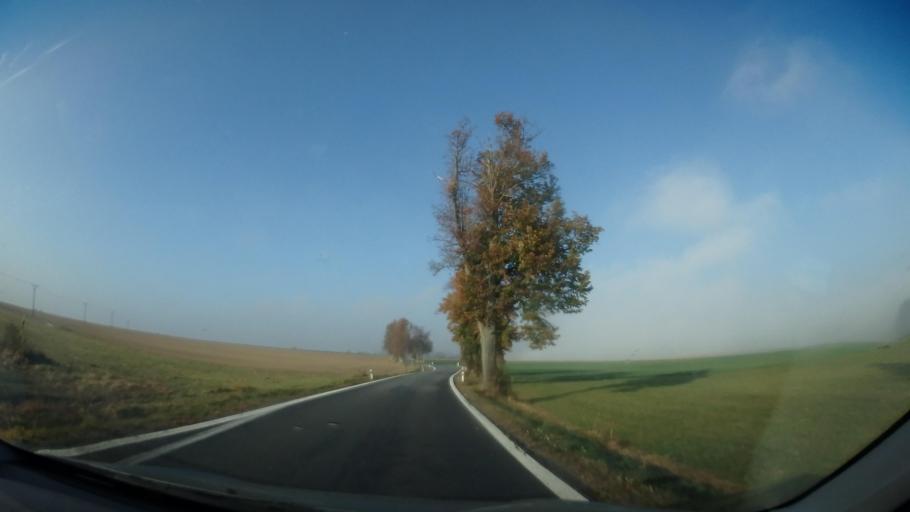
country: CZ
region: Vysocina
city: Krizanov
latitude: 49.4386
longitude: 16.1648
